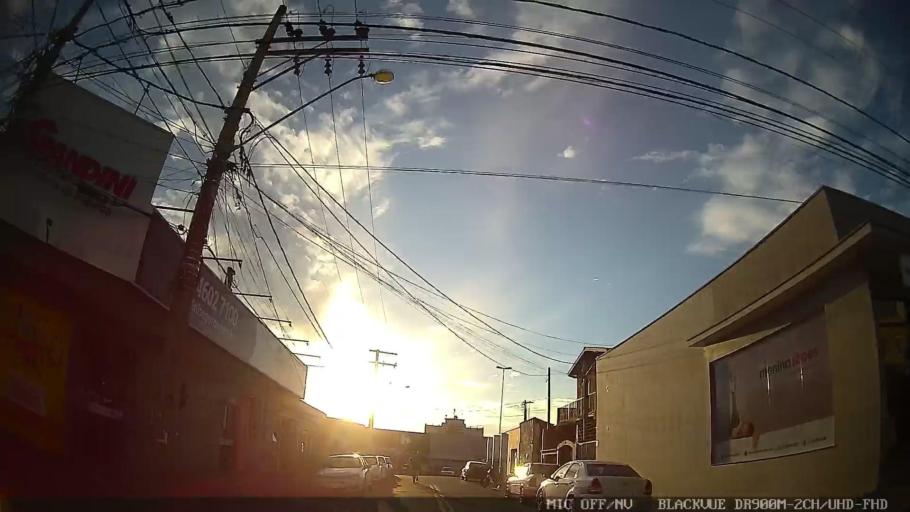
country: BR
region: Sao Paulo
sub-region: Salto
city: Salto
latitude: -23.2010
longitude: -47.2889
